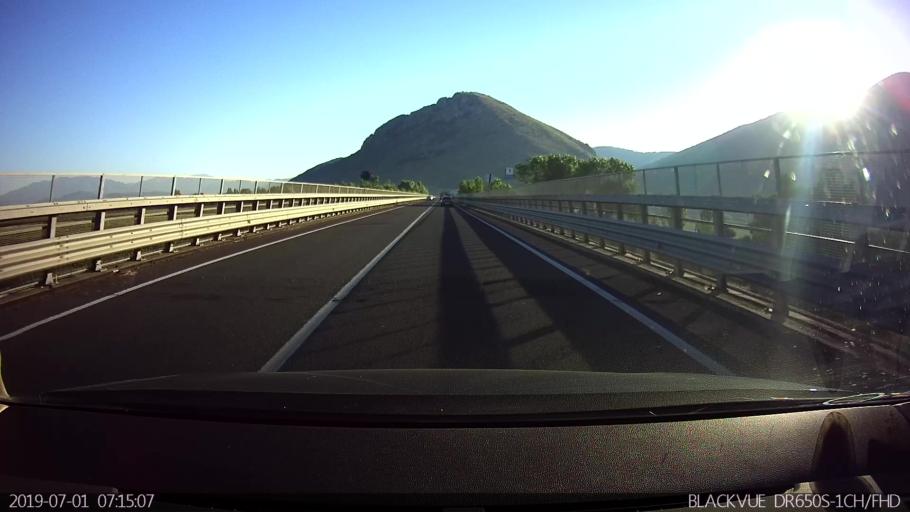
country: IT
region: Latium
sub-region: Provincia di Latina
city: Borgo Hermada
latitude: 41.3283
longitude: 13.1907
